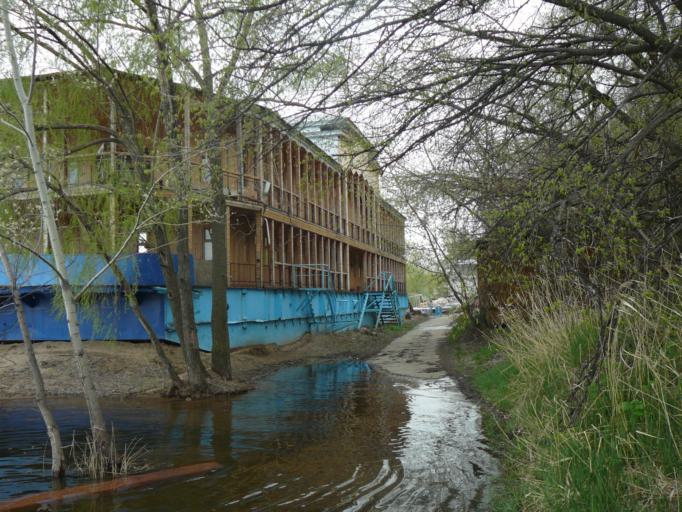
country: RU
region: Saratov
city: Shumeyka
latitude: 51.5935
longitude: 46.1848
